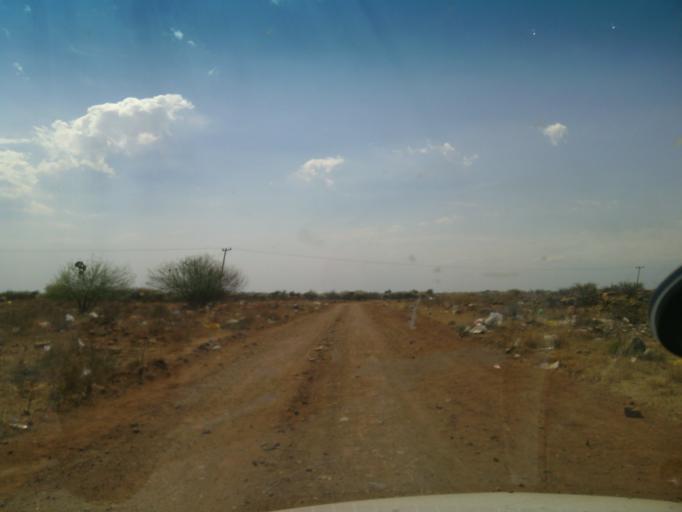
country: ZA
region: Northern Cape
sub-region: Frances Baard District Municipality
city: Barkly West
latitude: -28.5342
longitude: 24.4903
